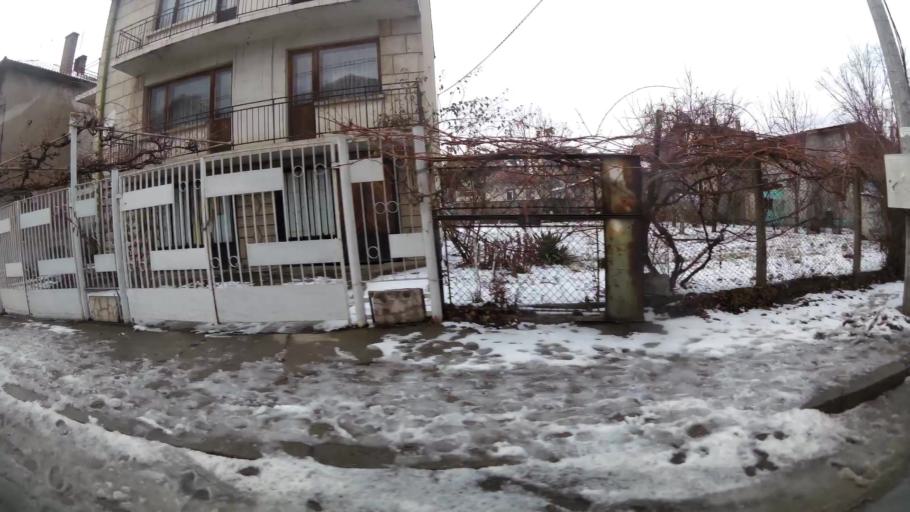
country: BG
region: Sofia-Capital
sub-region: Stolichna Obshtina
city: Sofia
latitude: 42.7190
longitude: 23.3451
